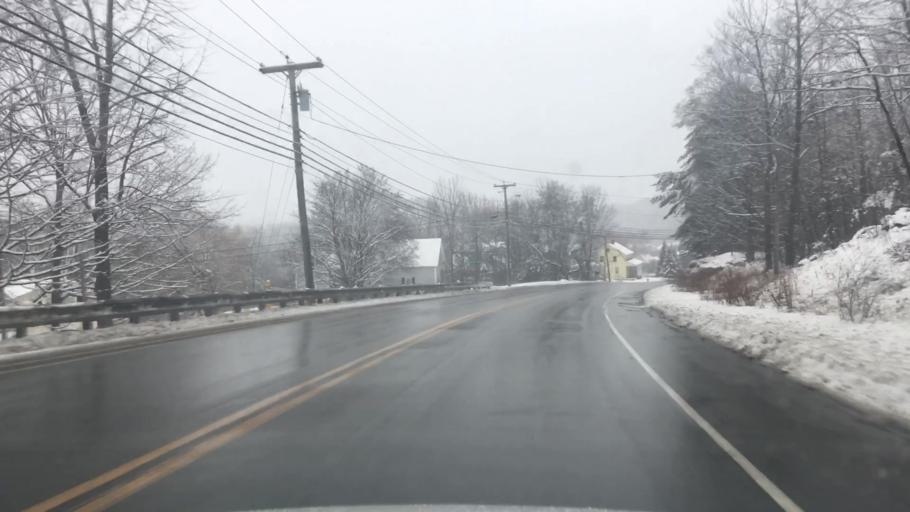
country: US
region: Maine
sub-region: Kennebec County
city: Chelsea
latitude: 44.2981
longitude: -69.7302
